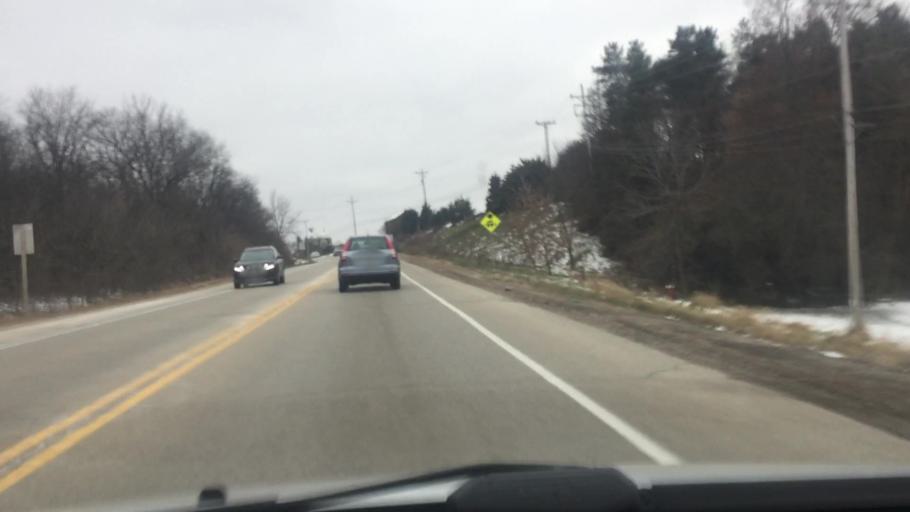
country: US
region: Wisconsin
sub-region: Waukesha County
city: Hartland
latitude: 43.0736
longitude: -88.3642
